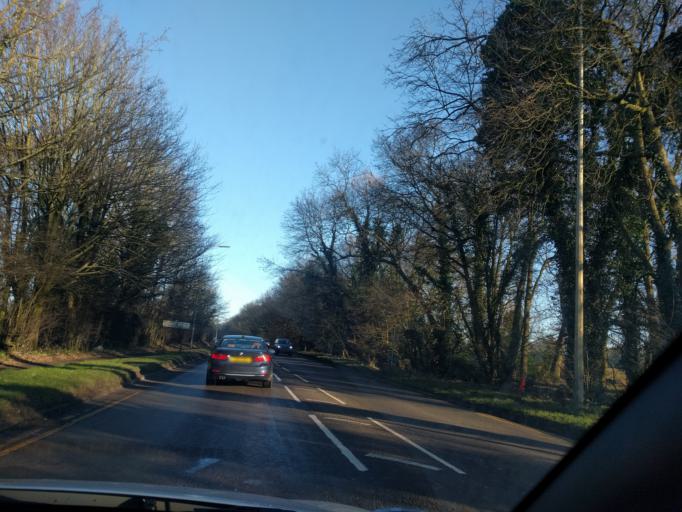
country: GB
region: England
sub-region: Staffordshire
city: Featherstone
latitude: 52.6483
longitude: -2.0826
